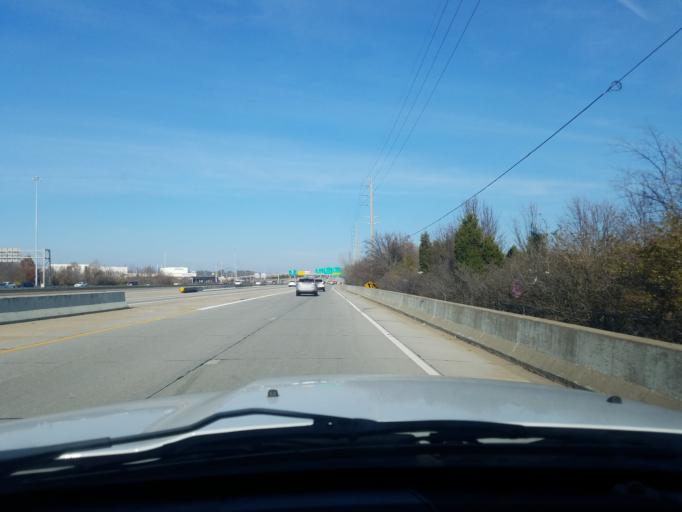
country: US
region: Kentucky
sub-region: Jefferson County
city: Saint Regis Park
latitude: 38.2420
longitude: -85.6215
